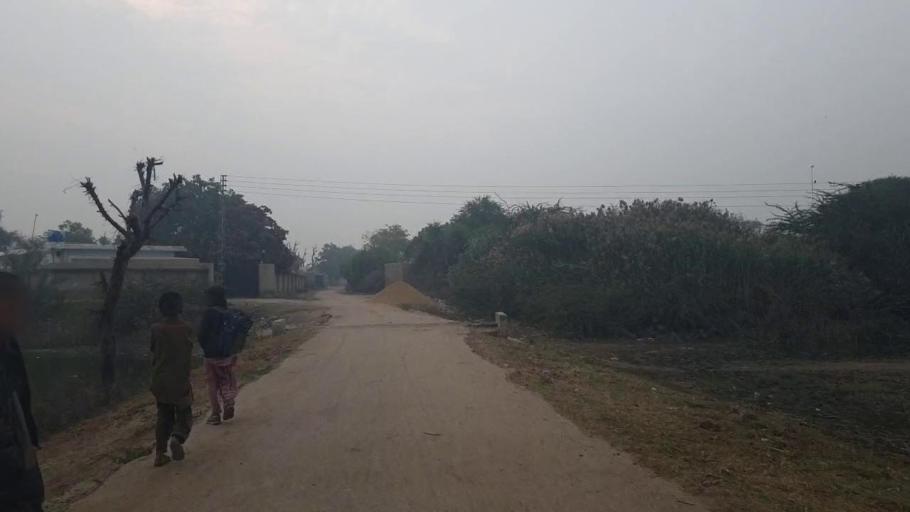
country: PK
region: Sindh
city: Tando Adam
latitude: 25.7317
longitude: 68.6724
